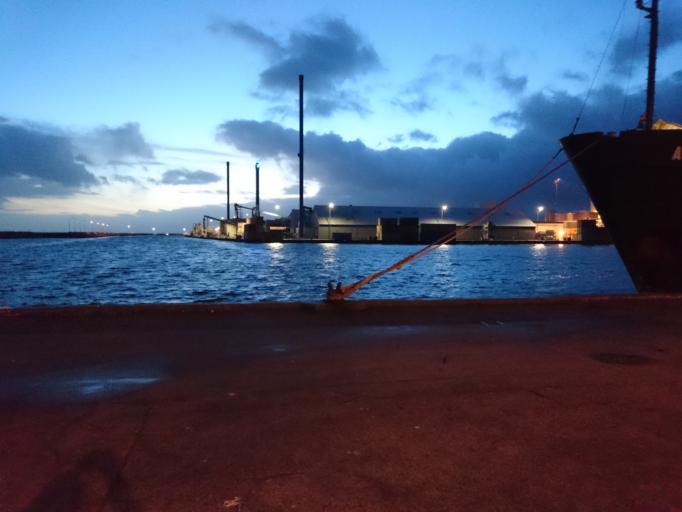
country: DK
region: North Denmark
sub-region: Frederikshavn Kommune
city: Skagen
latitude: 57.7206
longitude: 10.6037
